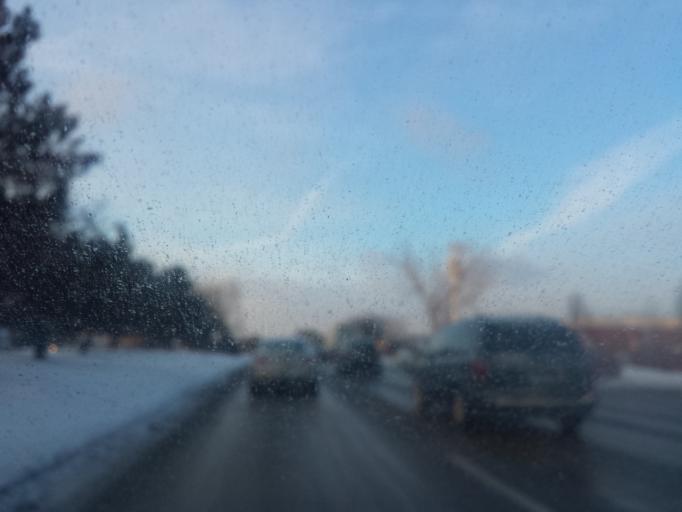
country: US
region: Michigan
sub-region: Oakland County
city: Bingham Farms
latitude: 42.5398
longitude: -83.2847
